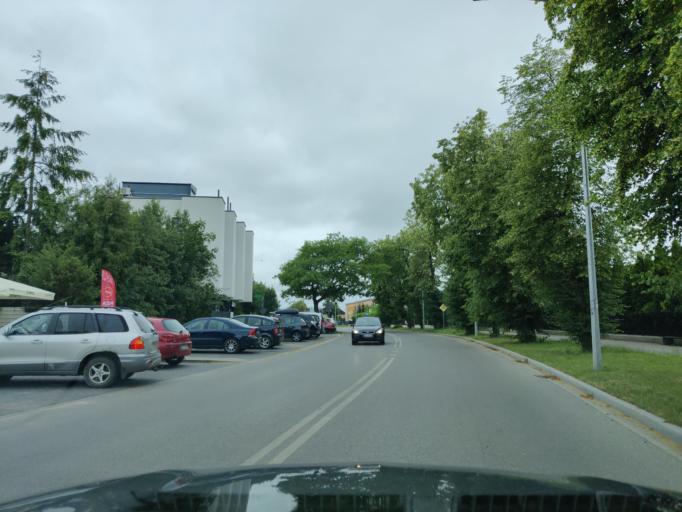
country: PL
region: Masovian Voivodeship
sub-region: Powiat pultuski
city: Pultusk
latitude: 52.7064
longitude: 21.0766
